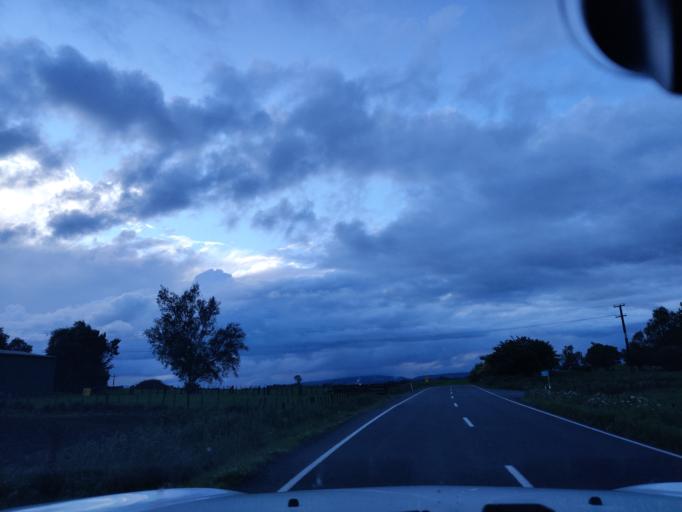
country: NZ
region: Waikato
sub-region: South Waikato District
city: Tokoroa
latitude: -38.2068
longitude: 175.8213
